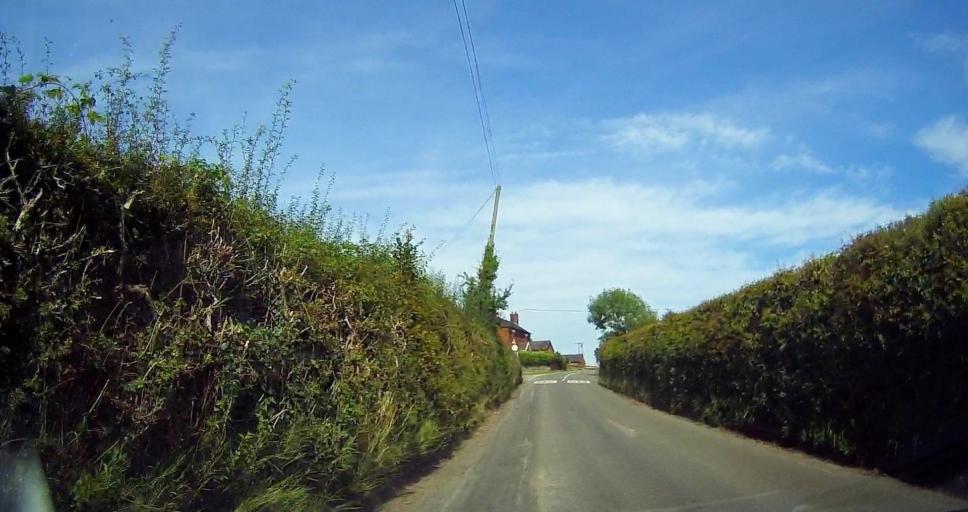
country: GB
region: England
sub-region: Shropshire
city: Market Drayton
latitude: 52.9736
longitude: -2.5189
